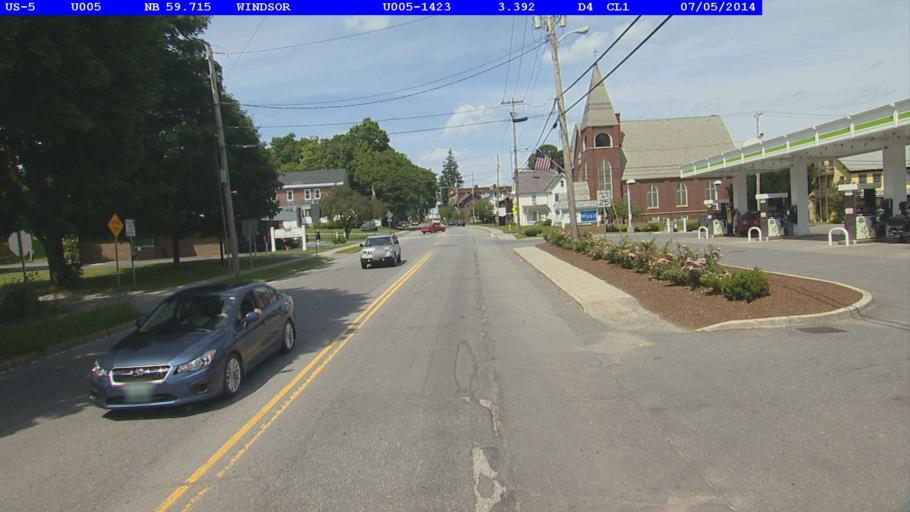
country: US
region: Vermont
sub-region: Windsor County
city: Windsor
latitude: 43.4759
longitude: -72.3882
